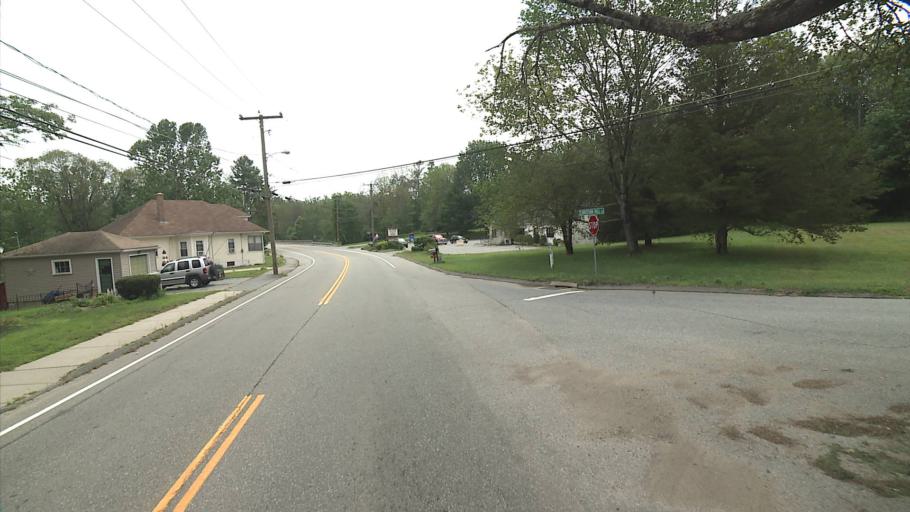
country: US
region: Connecticut
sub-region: Windham County
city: Wauregan
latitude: 41.7487
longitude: -71.9166
